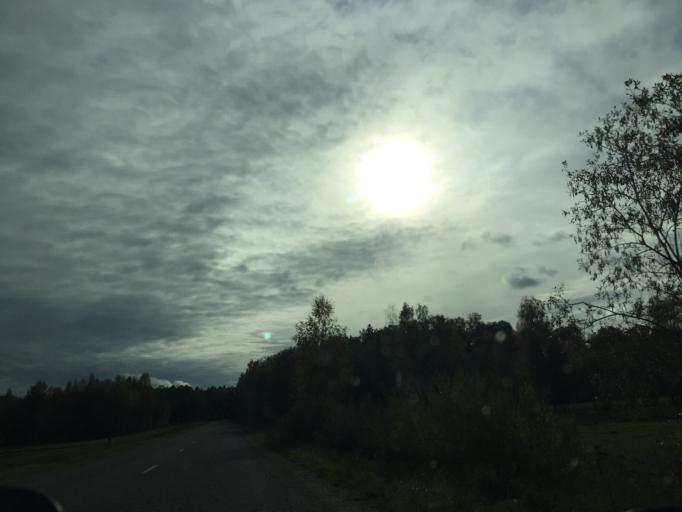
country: LV
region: Auces Novads
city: Auce
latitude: 56.5576
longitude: 23.0187
